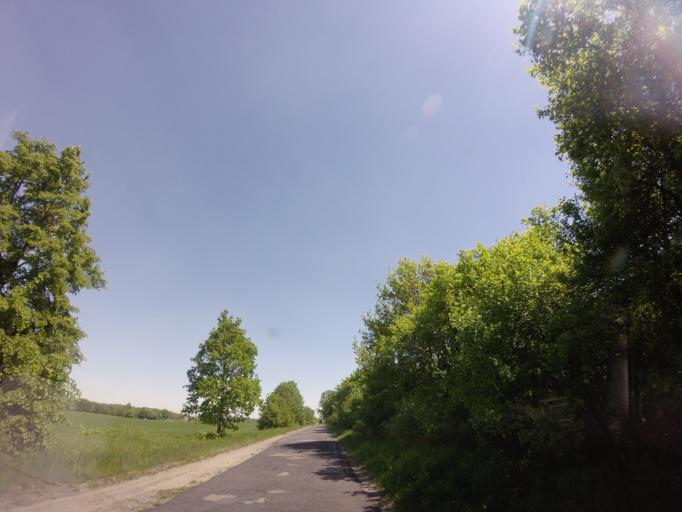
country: PL
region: West Pomeranian Voivodeship
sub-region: Powiat mysliborski
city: Nowogrodek Pomorski
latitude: 52.9111
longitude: 15.0897
